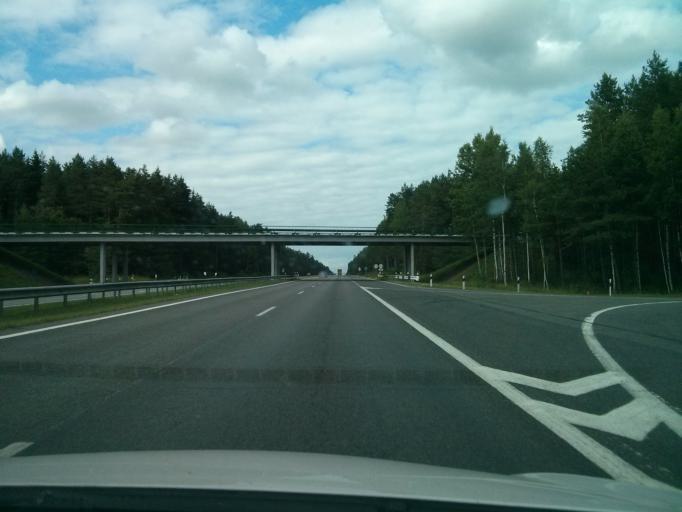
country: BY
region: Minsk
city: Zamostochcha
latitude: 53.8914
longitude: 27.9419
